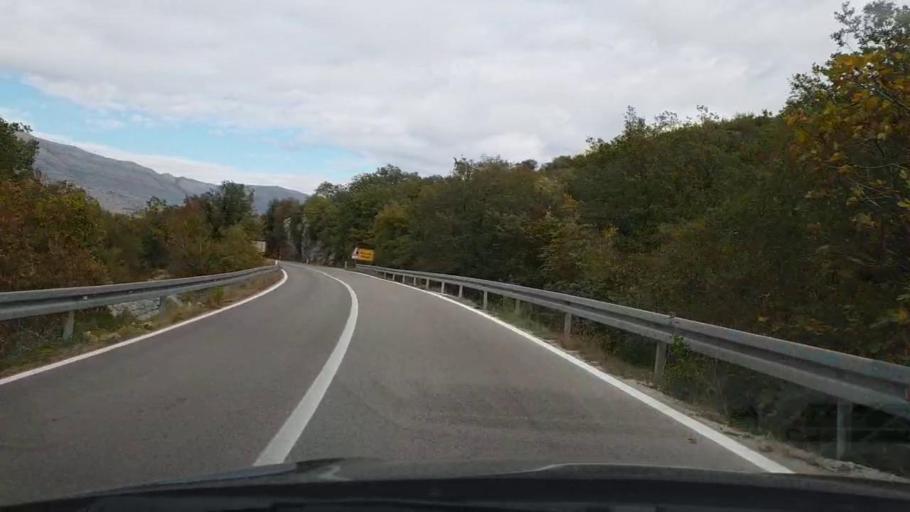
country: BA
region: Republika Srpska
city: Trebinje
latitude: 42.6812
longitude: 18.3010
